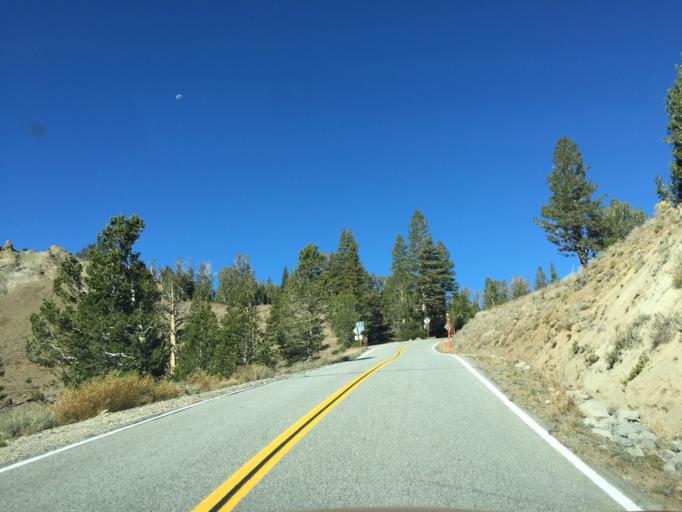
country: US
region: California
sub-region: Mono County
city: Bridgeport
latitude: 38.3275
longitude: -119.6360
